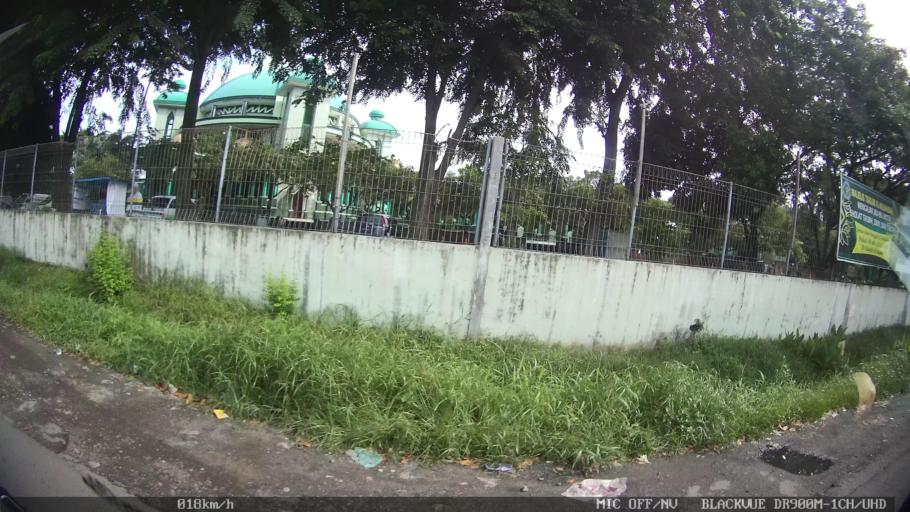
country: ID
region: North Sumatra
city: Medan
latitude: 3.6293
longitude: 98.6948
